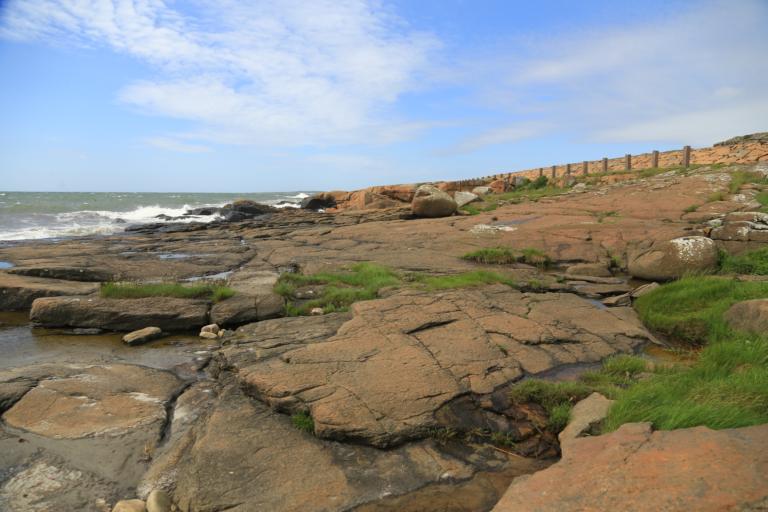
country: SE
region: Halland
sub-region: Varbergs Kommun
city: Varberg
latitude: 57.0906
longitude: 12.2419
